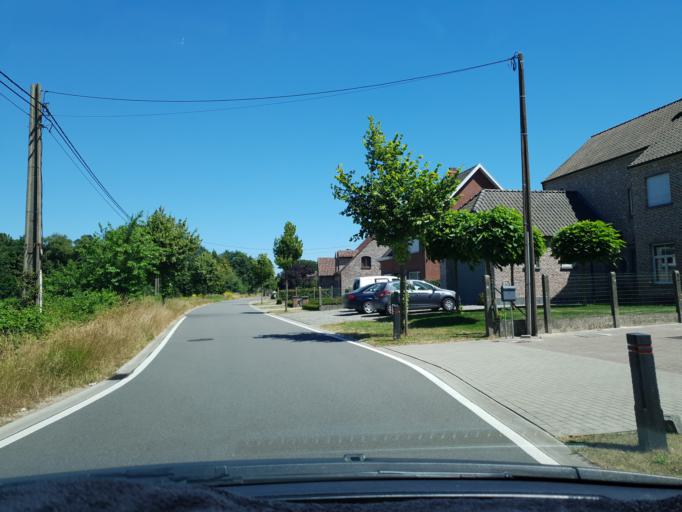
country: BE
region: Flanders
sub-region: Provincie Antwerpen
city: Olen
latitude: 51.1544
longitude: 4.9120
